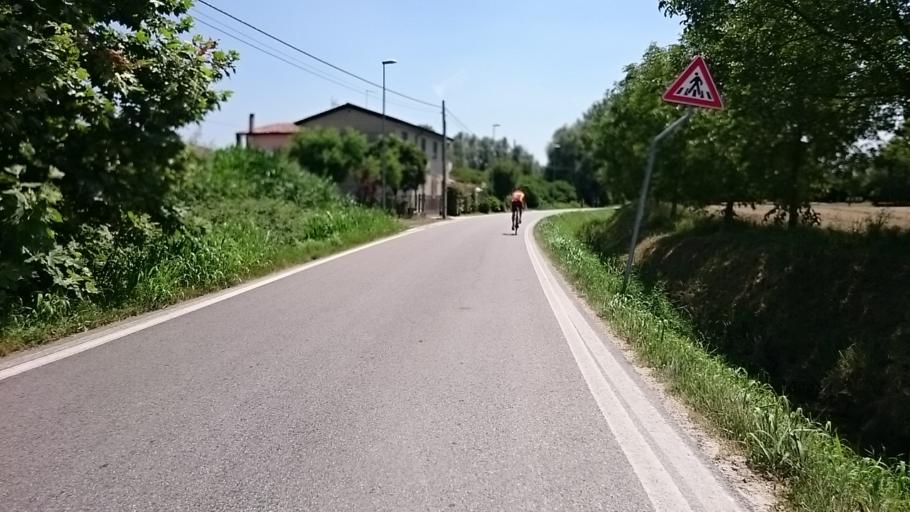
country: IT
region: Veneto
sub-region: Provincia di Padova
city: Vigonza
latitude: 45.4499
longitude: 11.9711
